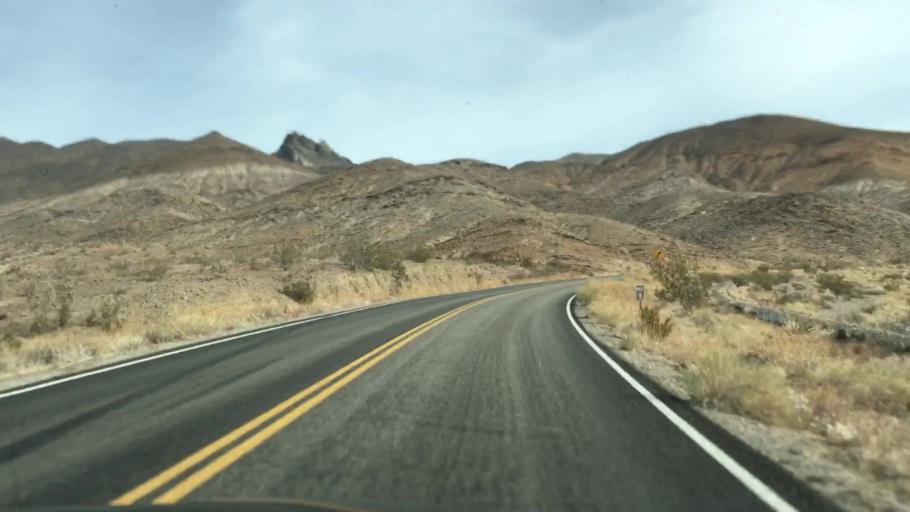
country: US
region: Nevada
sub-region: Nye County
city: Beatty
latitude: 36.7470
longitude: -116.9539
